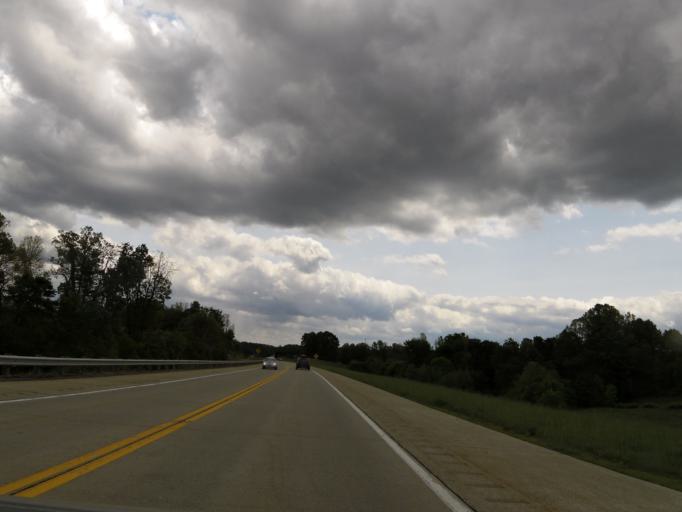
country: US
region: Ohio
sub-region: Meigs County
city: Pomeroy
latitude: 39.1551
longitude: -82.0336
